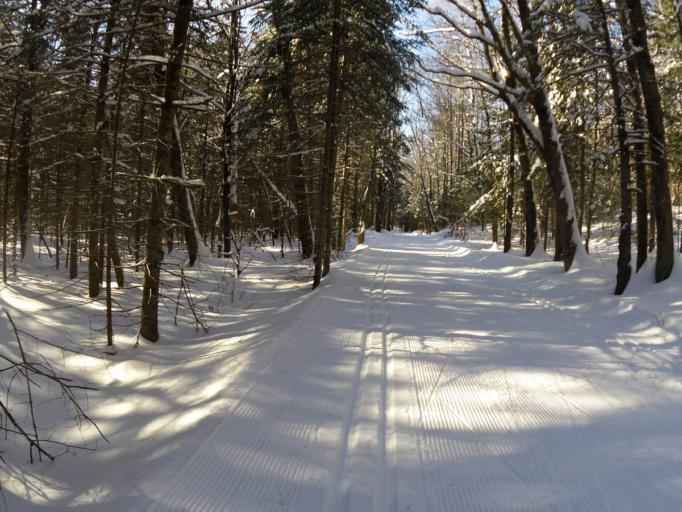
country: CA
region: Quebec
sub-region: Outaouais
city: Wakefield
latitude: 45.6279
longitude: -75.9755
